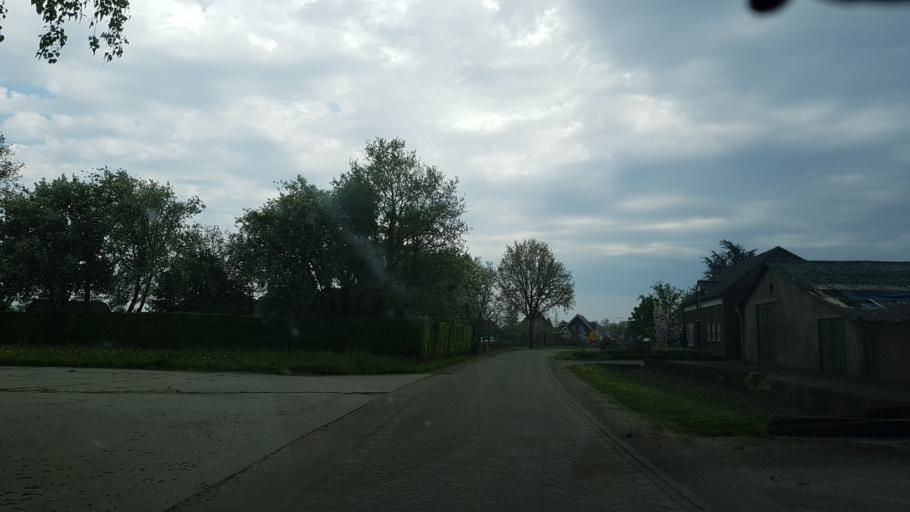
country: NL
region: North Brabant
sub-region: Gemeente Someren
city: Someren
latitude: 51.3756
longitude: 5.6895
